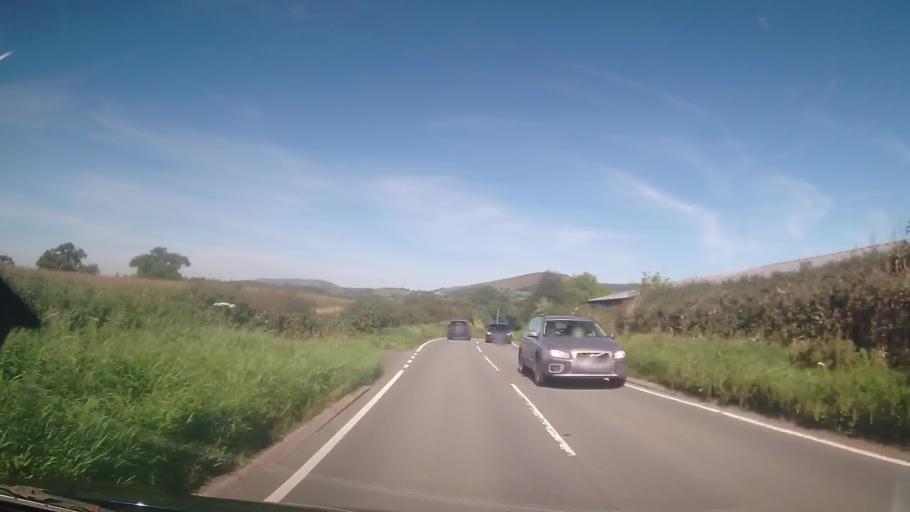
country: GB
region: England
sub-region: Shropshire
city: Lydham
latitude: 52.5091
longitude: -2.9834
